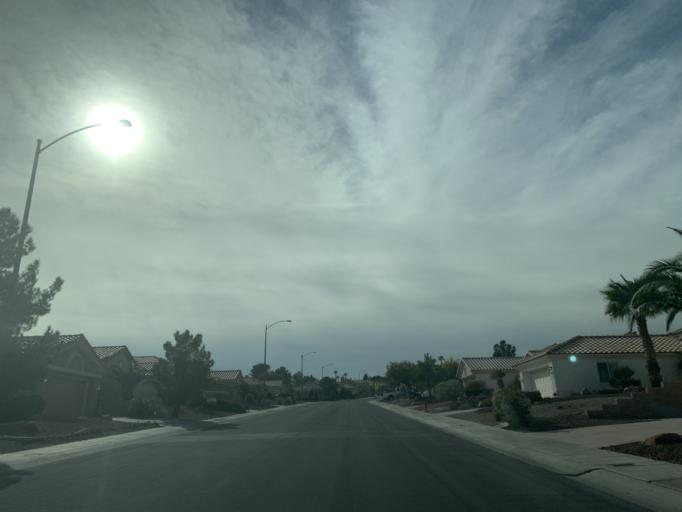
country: US
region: Nevada
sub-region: Clark County
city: Summerlin South
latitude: 36.2148
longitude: -115.3292
